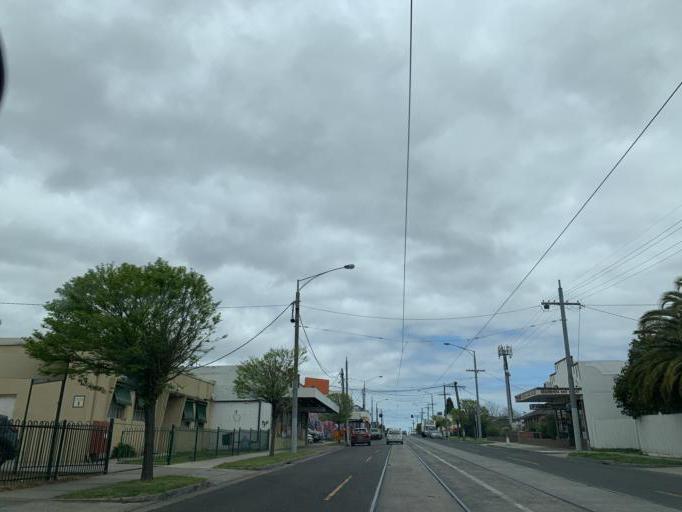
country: AU
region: Victoria
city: Thornbury
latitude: -37.7350
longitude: 144.9906
